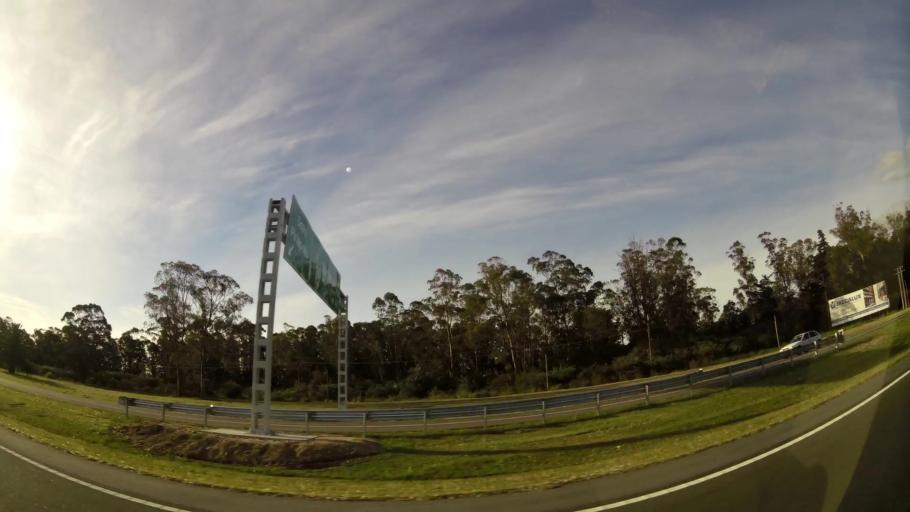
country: UY
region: Maldonado
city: Piriapolis
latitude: -34.7852
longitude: -55.3677
